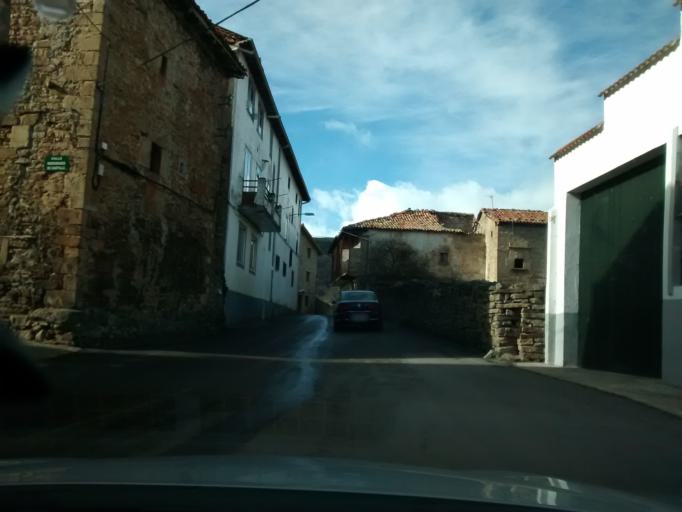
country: ES
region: Castille and Leon
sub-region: Provincia de Burgos
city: Espinosa de los Monteros
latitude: 43.0770
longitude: -3.5483
